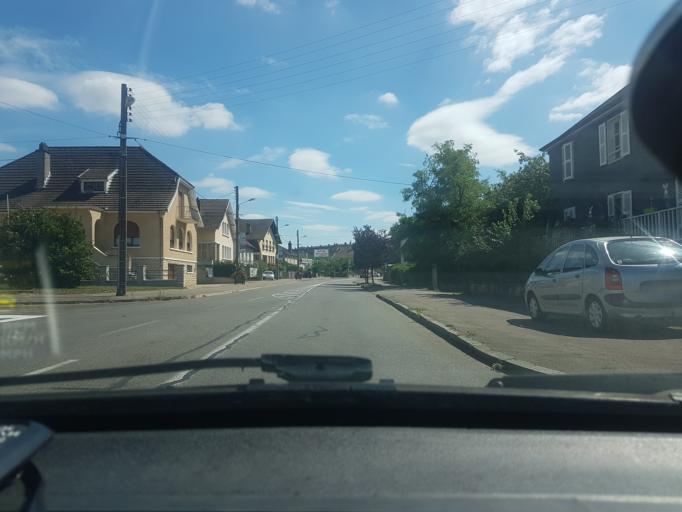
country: FR
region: Franche-Comte
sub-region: Departement de la Haute-Saone
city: Gray
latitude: 47.4476
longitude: 5.5958
